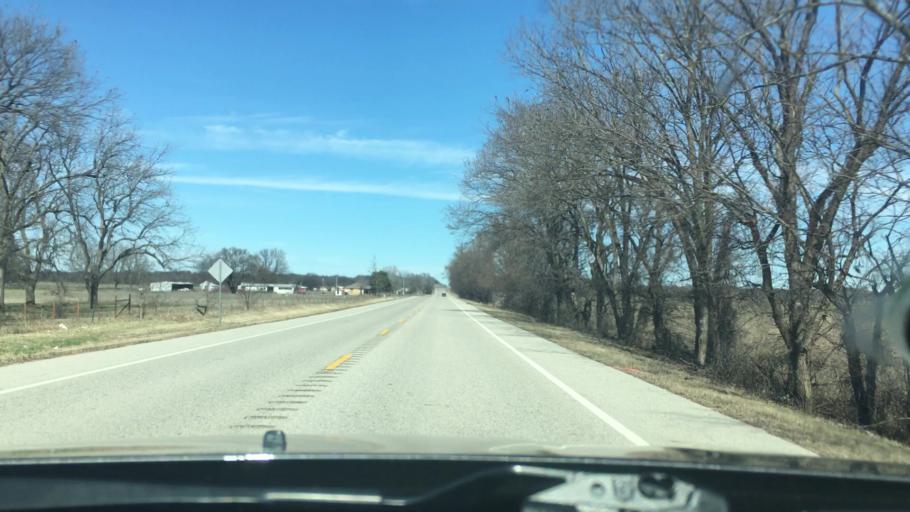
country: US
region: Oklahoma
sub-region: Murray County
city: Sulphur
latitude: 34.3919
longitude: -96.9511
